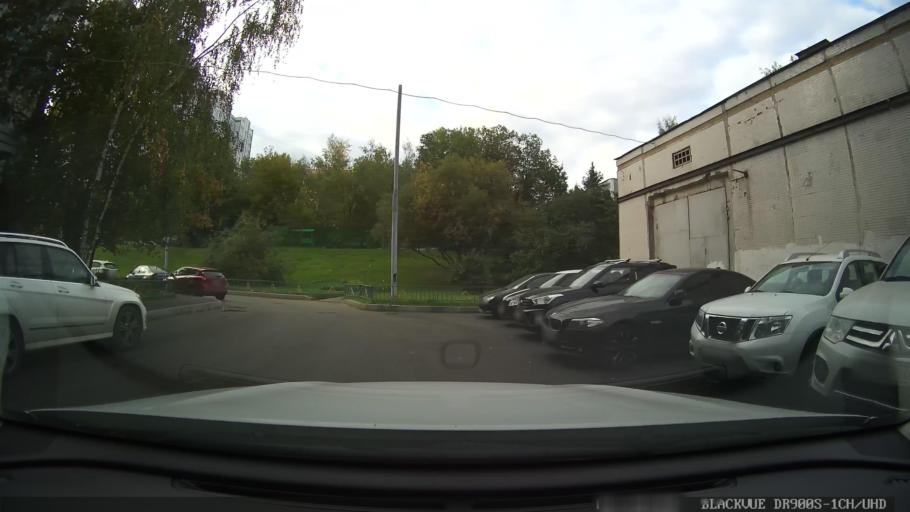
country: RU
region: Moskovskaya
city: Bol'shaya Setun'
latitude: 55.7585
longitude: 37.4046
